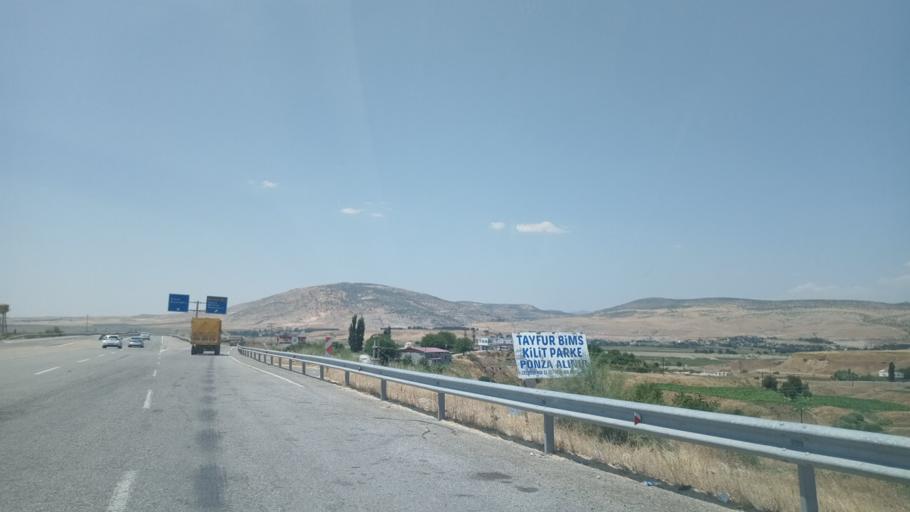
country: TR
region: Diyarbakir
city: Malabadi
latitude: 38.1345
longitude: 41.2299
